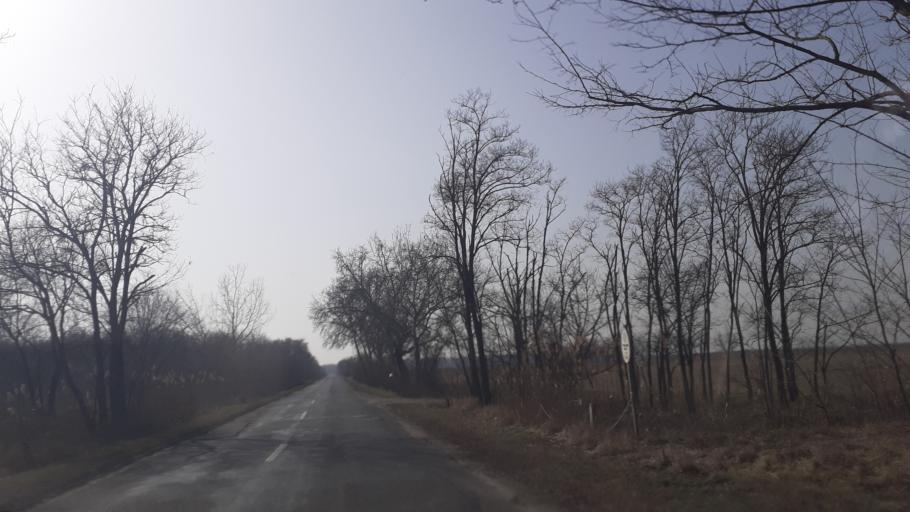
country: HU
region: Bacs-Kiskun
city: Kunszentmiklos
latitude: 47.0528
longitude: 19.2354
